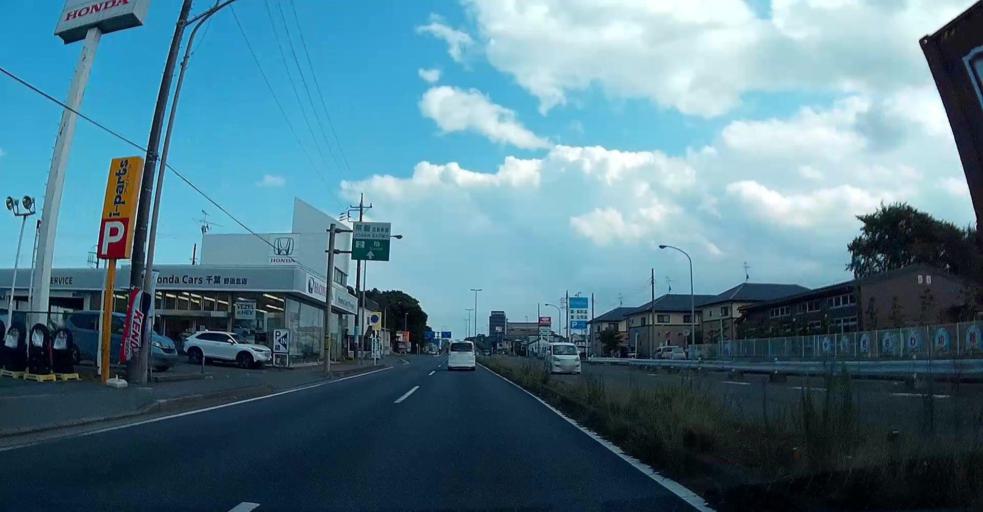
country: JP
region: Chiba
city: Noda
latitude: 35.9614
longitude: 139.8710
